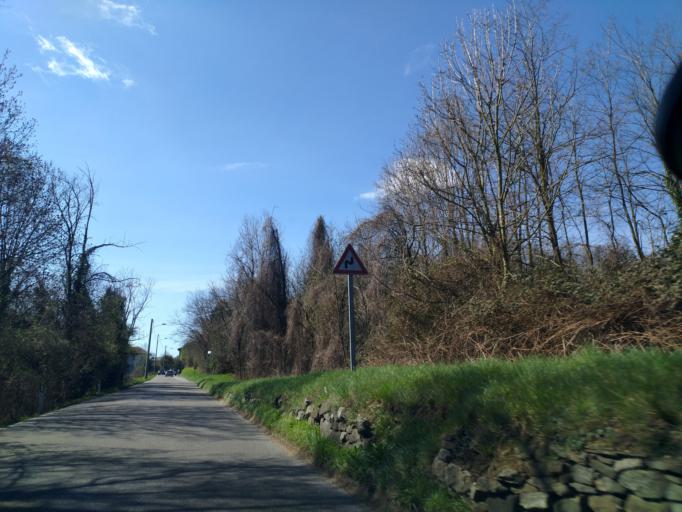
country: IT
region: Lombardy
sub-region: Provincia di Como
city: Anzano del Parco
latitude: 45.7602
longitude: 9.1985
